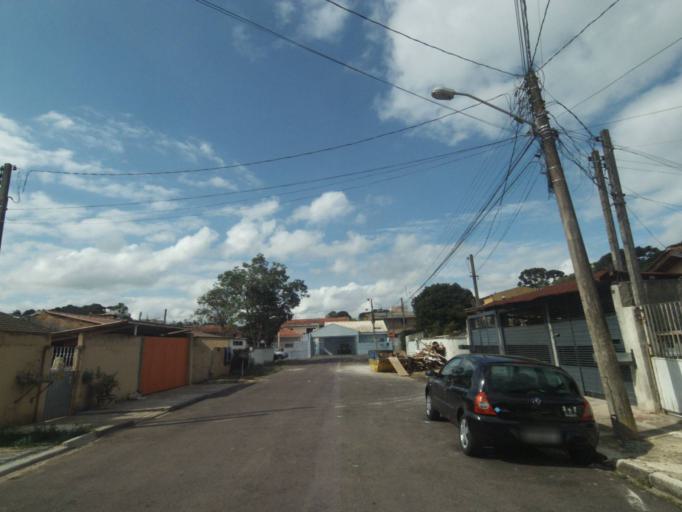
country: BR
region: Parana
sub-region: Curitiba
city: Curitiba
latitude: -25.3827
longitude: -49.3008
